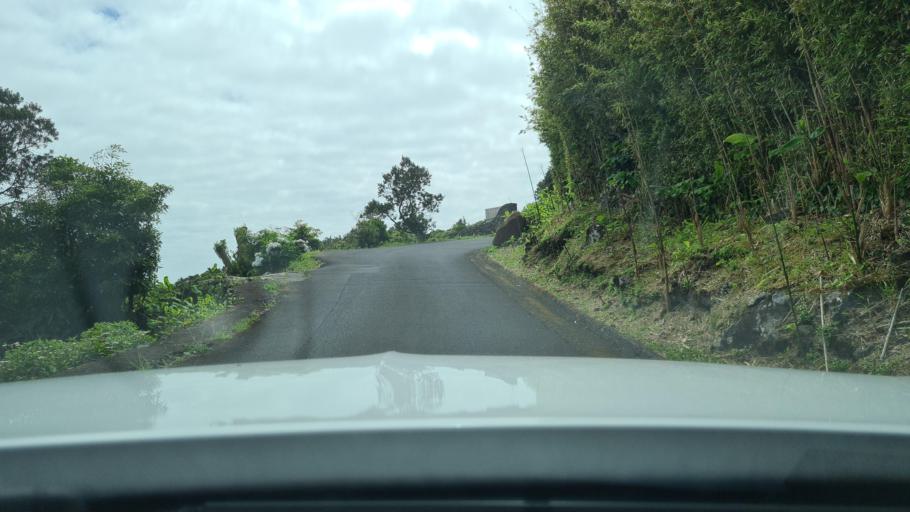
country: PT
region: Azores
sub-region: Sao Roque do Pico
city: Sao Roque do Pico
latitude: 38.6388
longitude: -27.9666
